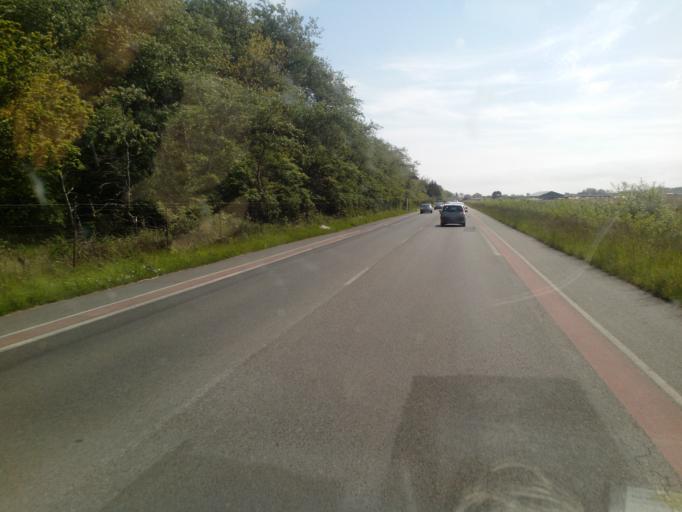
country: FR
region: Nord-Pas-de-Calais
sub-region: Departement du Pas-de-Calais
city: Berck
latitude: 50.4262
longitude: 1.6020
